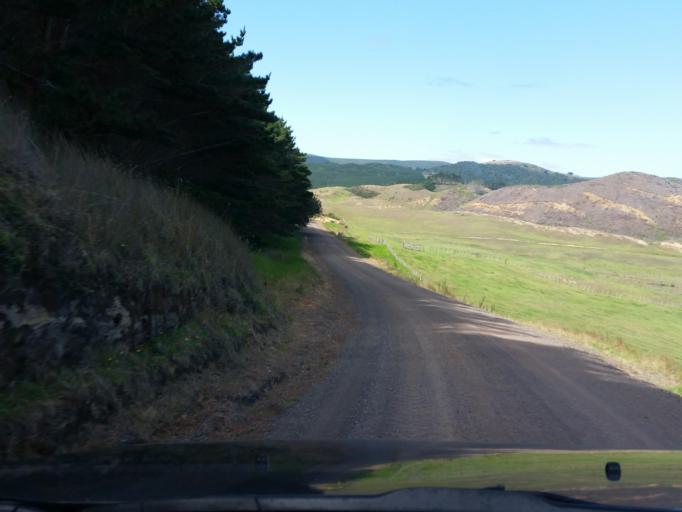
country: NZ
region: Northland
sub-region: Kaipara District
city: Dargaville
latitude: -35.7027
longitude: 173.5239
